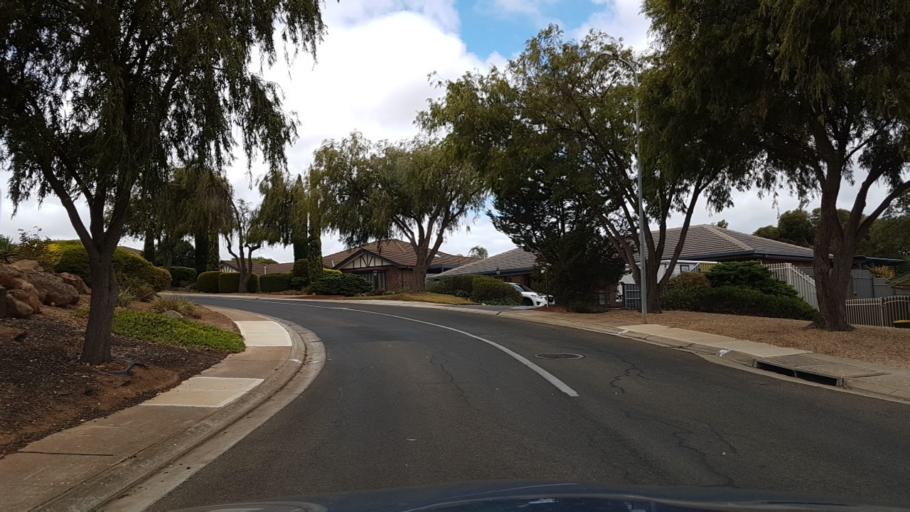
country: AU
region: South Australia
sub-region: Gawler
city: Gawler
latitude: -34.6062
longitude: 138.7605
